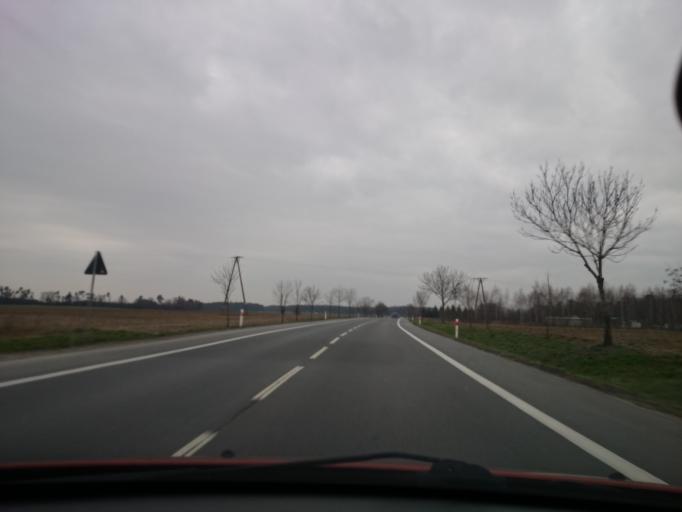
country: PL
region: Opole Voivodeship
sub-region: Powiat nyski
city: Lambinowice
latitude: 50.5942
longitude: 17.5256
